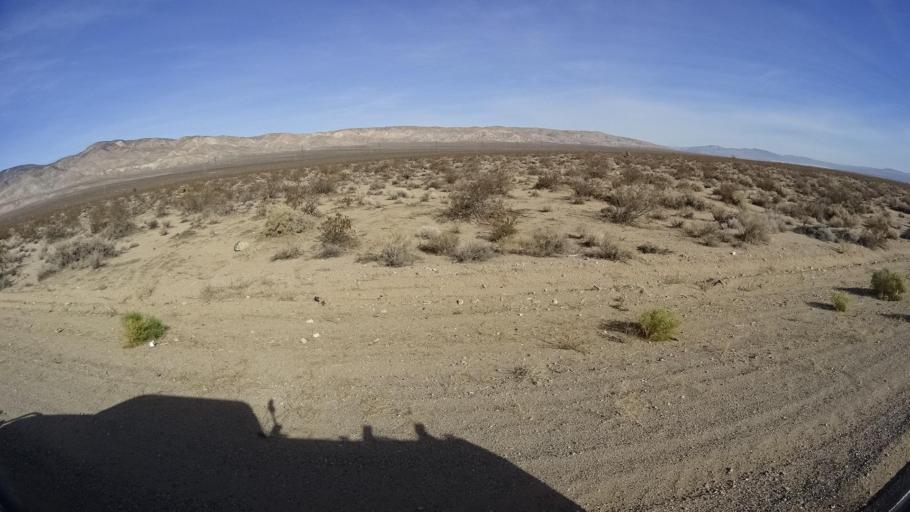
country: US
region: California
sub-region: Kern County
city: Mojave
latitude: 35.1254
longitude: -118.1403
